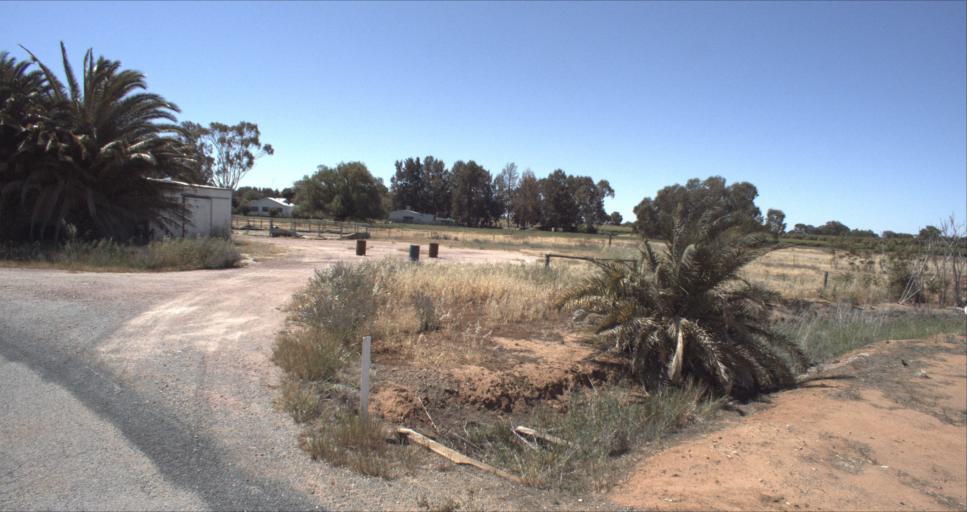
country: AU
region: New South Wales
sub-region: Leeton
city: Leeton
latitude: -34.5263
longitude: 146.3334
